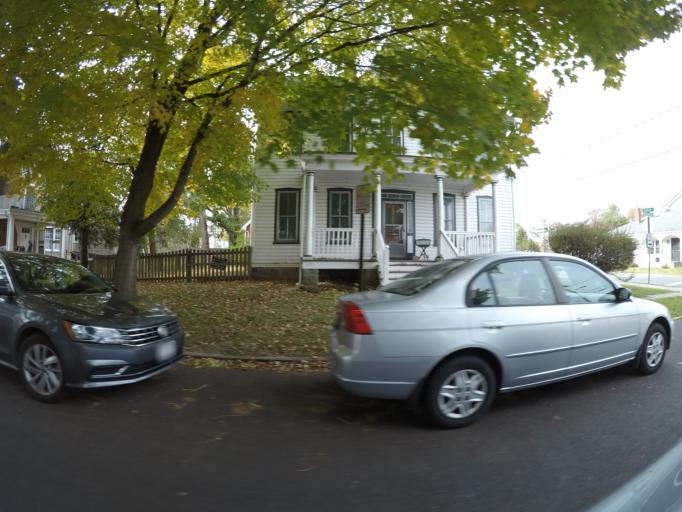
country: US
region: Maryland
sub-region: Harford County
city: Havre de Grace
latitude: 39.5464
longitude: -76.0897
